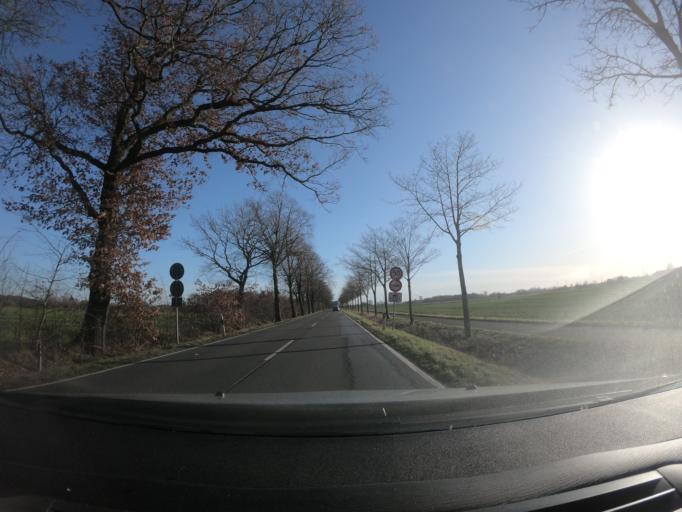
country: DE
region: North Rhine-Westphalia
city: Datteln
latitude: 51.6611
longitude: 7.4039
